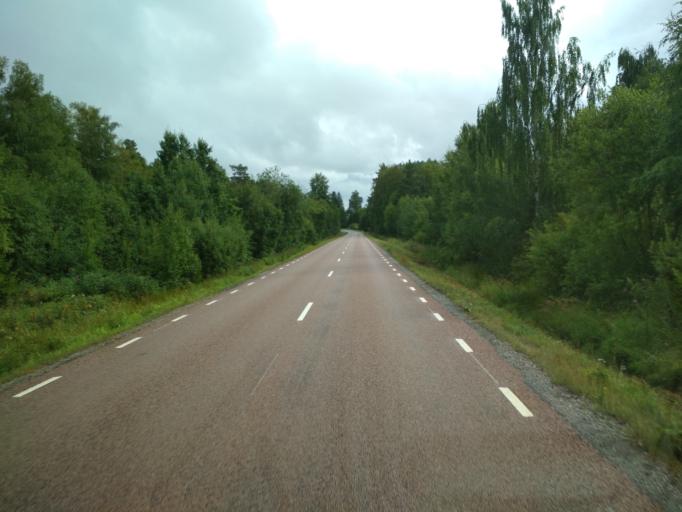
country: SE
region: Vaestmanland
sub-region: Surahammars Kommun
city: Ramnas
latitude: 59.7988
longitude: 16.1731
